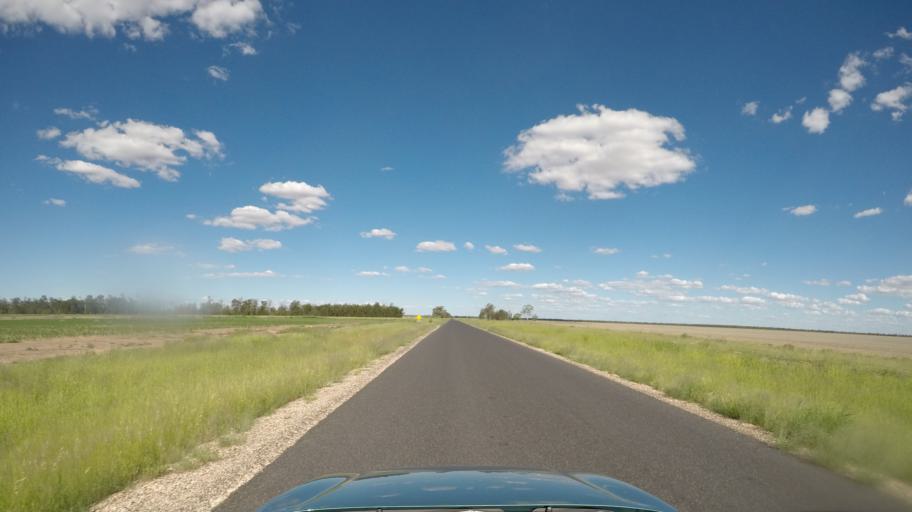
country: AU
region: Queensland
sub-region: Goondiwindi
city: Goondiwindi
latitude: -28.1754
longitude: 150.2530
